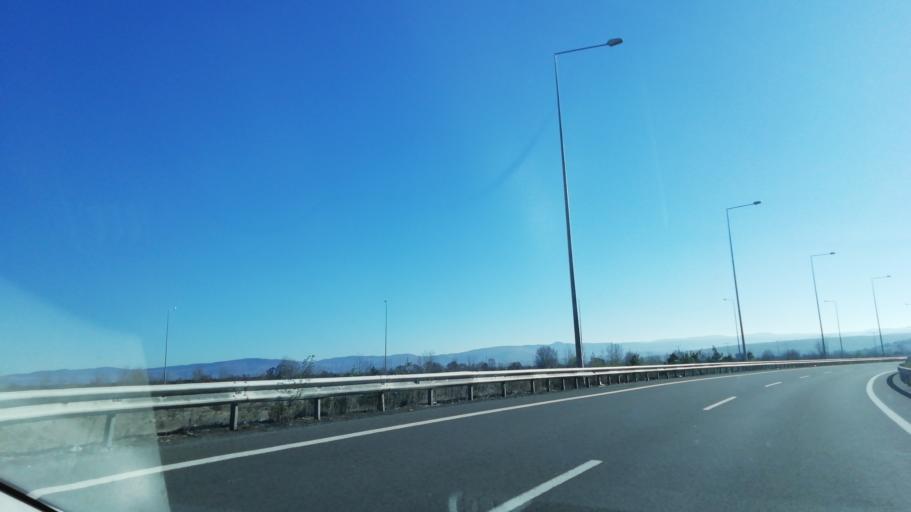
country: TR
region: Bolu
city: Gerede
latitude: 40.7373
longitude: 32.1849
